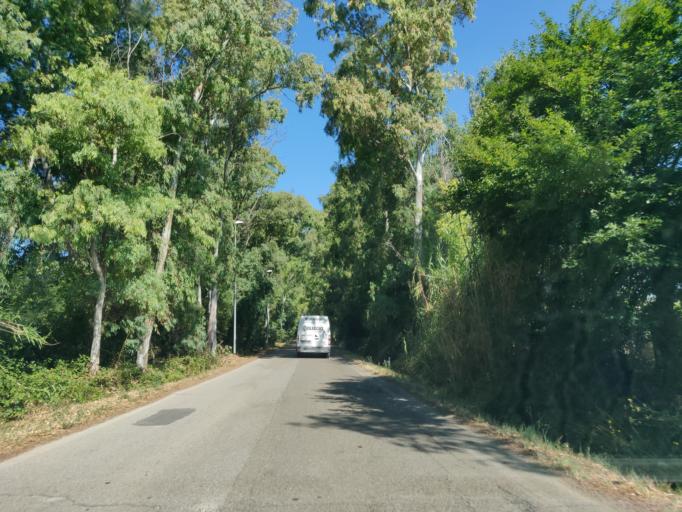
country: IT
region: Latium
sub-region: Citta metropolitana di Roma Capitale
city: Aurelia
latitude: 42.1591
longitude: 11.7500
